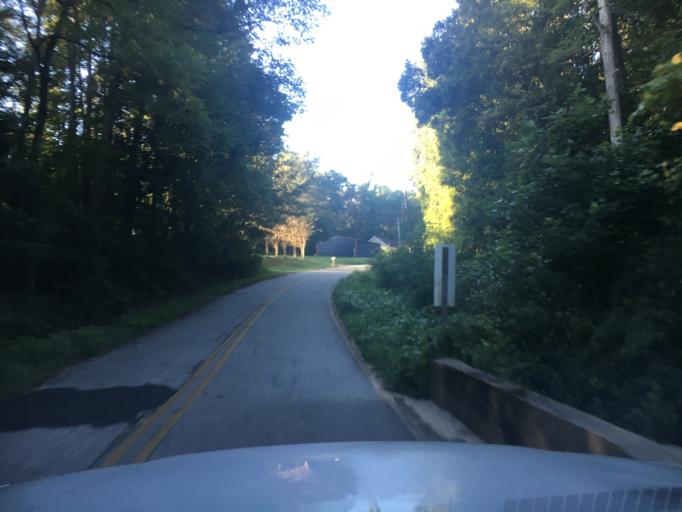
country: US
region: South Carolina
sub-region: Spartanburg County
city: Woodruff
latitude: 34.6682
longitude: -81.9638
